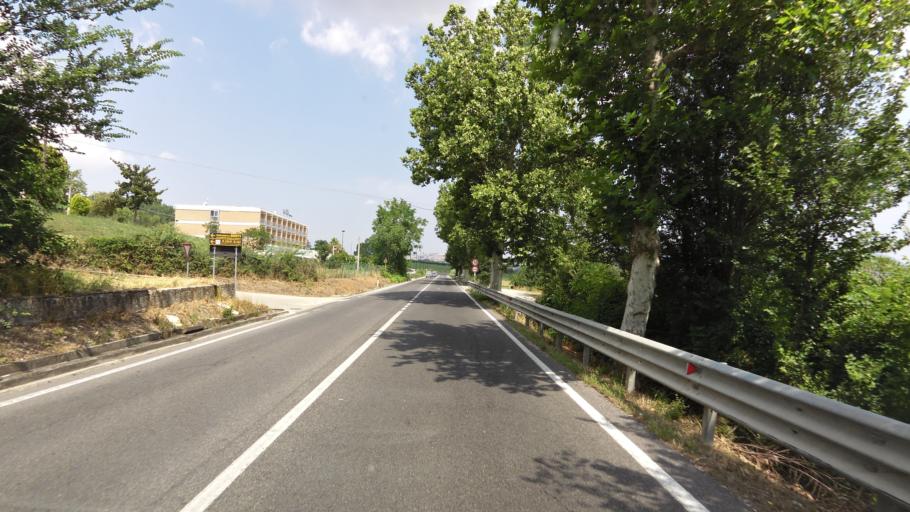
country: IT
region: The Marches
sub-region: Provincia di Ancona
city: Castelfidardo
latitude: 43.4794
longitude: 13.5795
